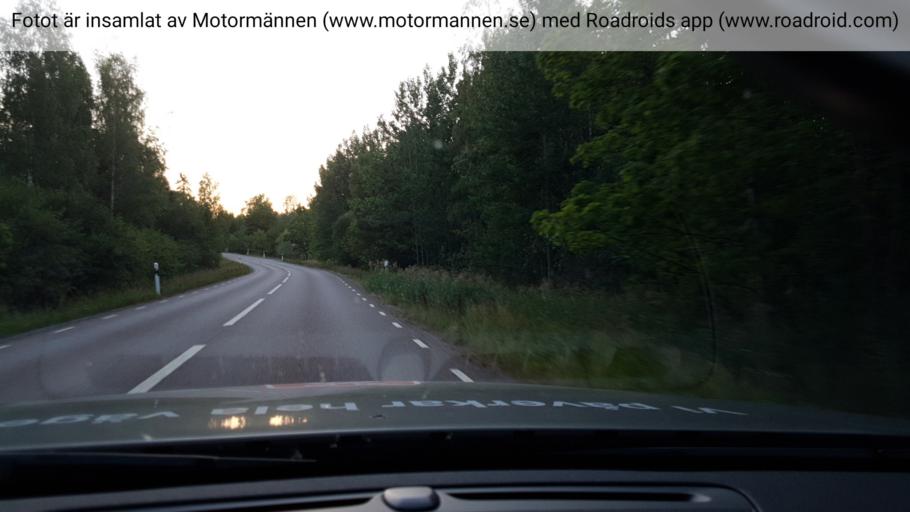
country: SE
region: Uppsala
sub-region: Heby Kommun
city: OEstervala
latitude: 60.0329
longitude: 17.2701
